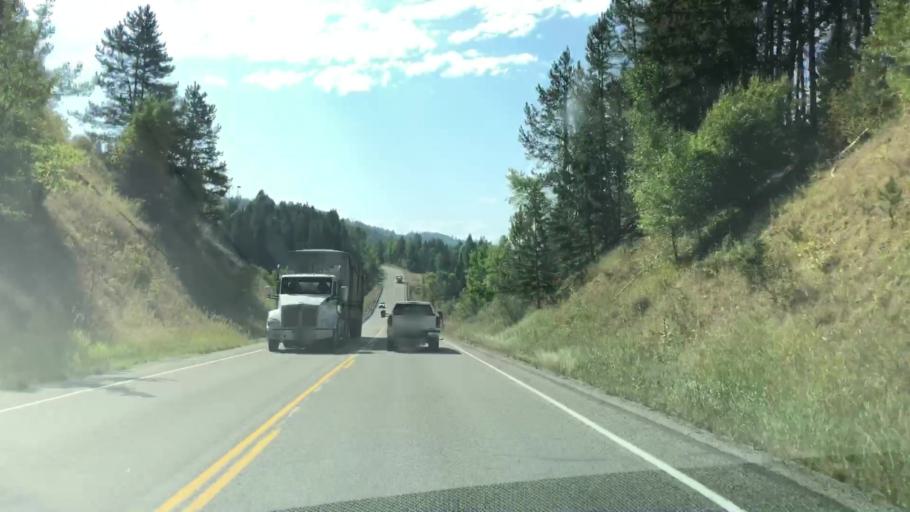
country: US
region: Idaho
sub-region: Teton County
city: Victor
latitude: 43.2854
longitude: -111.1207
